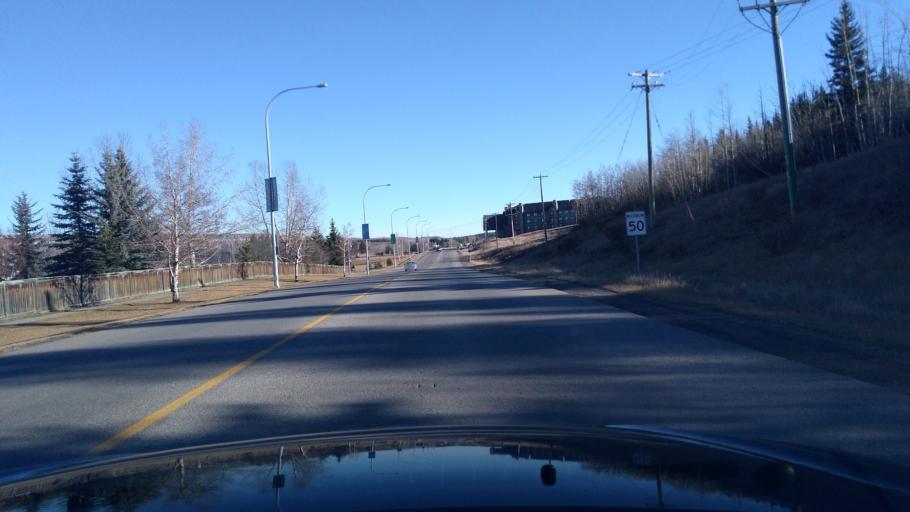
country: CA
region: Alberta
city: Cochrane
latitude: 51.1836
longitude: -114.4966
